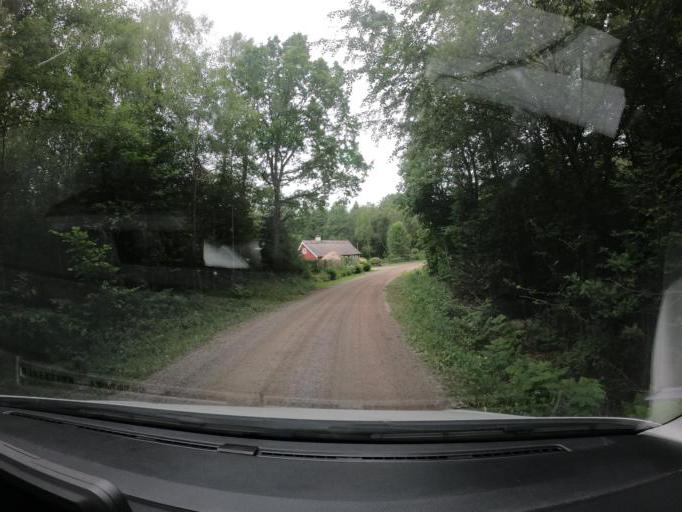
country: SE
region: Skane
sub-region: Perstorps Kommun
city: Perstorp
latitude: 56.1786
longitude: 13.5107
